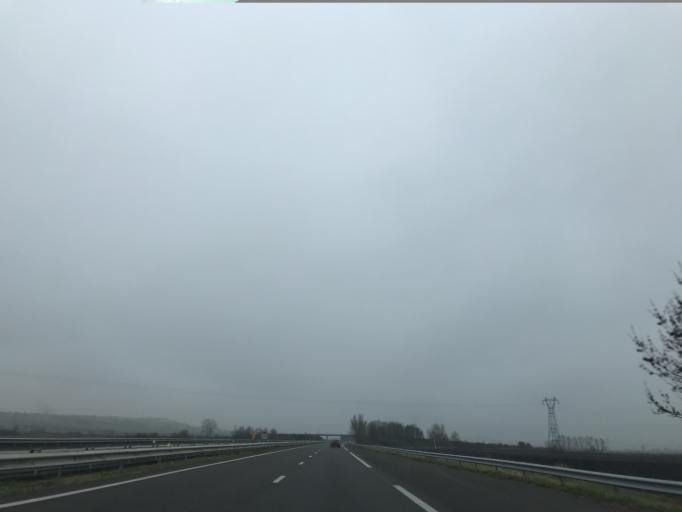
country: FR
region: Auvergne
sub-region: Departement du Puy-de-Dome
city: Pont-du-Chateau
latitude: 45.8212
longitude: 3.2242
